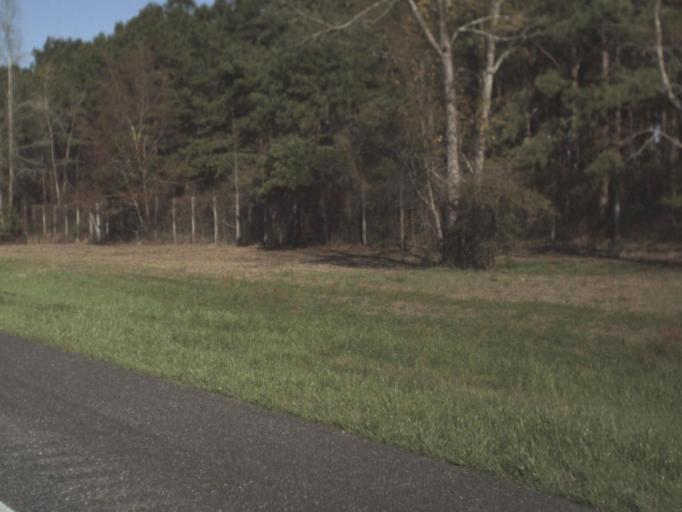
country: US
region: Florida
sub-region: Jefferson County
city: Monticello
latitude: 30.4787
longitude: -83.9374
